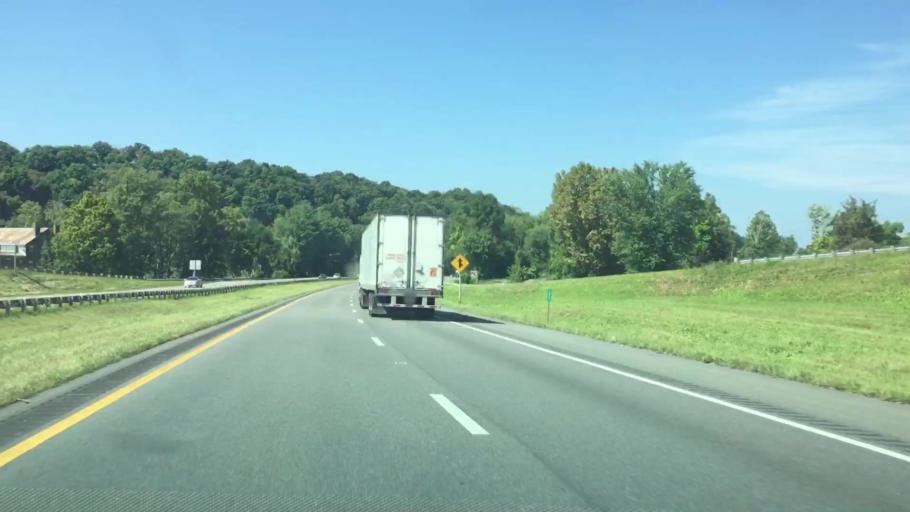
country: US
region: Virginia
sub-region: Smyth County
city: Adwolf
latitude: 36.8089
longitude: -81.6187
